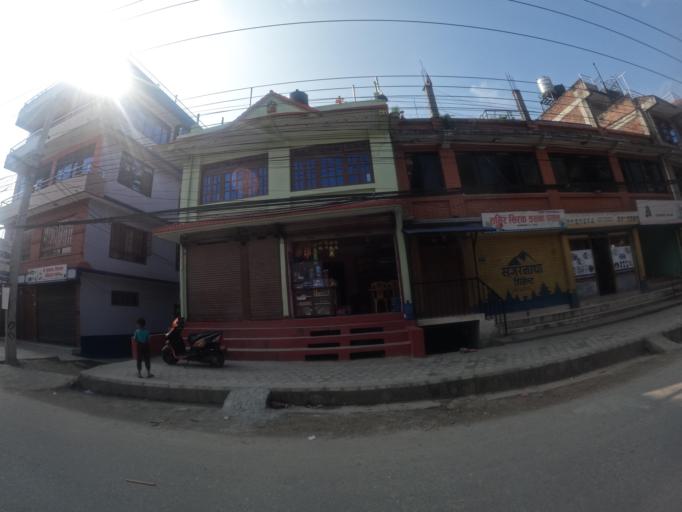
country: NP
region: Central Region
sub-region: Bagmati Zone
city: Bhaktapur
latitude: 27.6792
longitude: 85.4444
